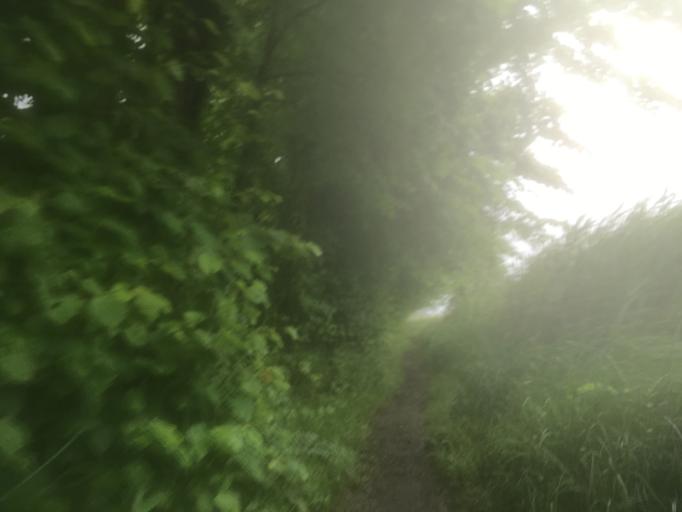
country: DE
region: Brandenburg
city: Zehdenick
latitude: 52.9907
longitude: 13.3334
